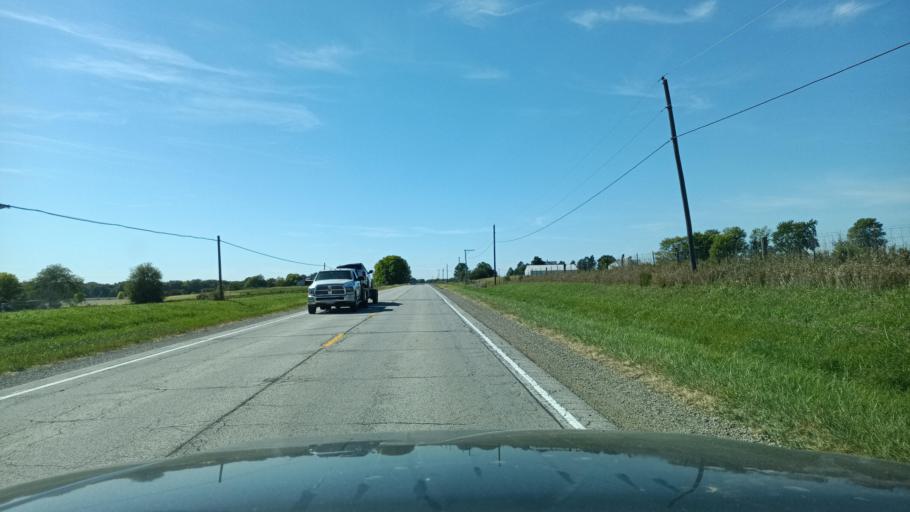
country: US
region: Illinois
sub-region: De Witt County
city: Farmer City
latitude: 40.2322
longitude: -88.6673
